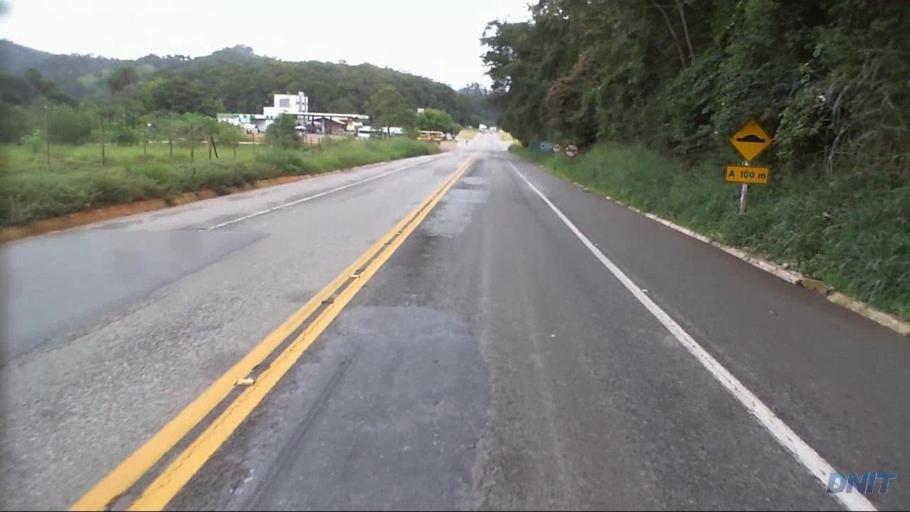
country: BR
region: Minas Gerais
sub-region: Joao Monlevade
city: Joao Monlevade
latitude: -19.8366
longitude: -43.3451
